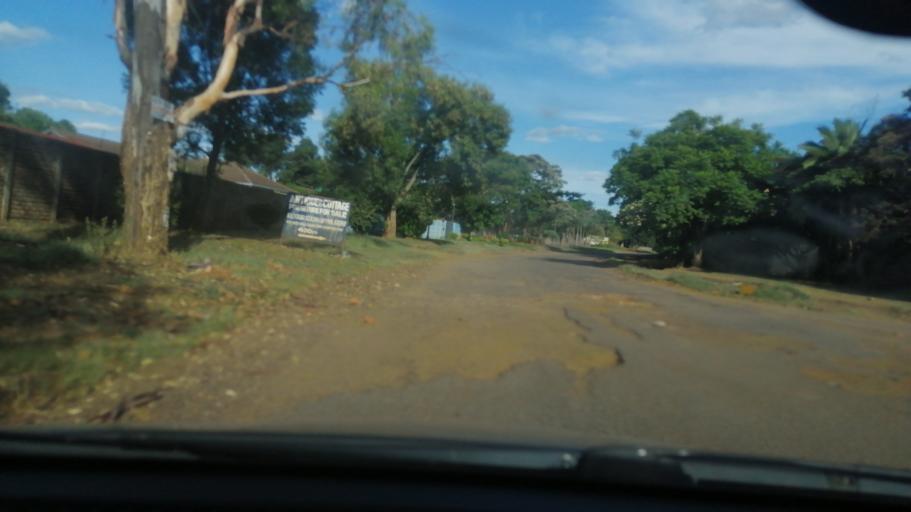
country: ZW
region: Harare
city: Harare
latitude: -17.7637
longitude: 31.0658
